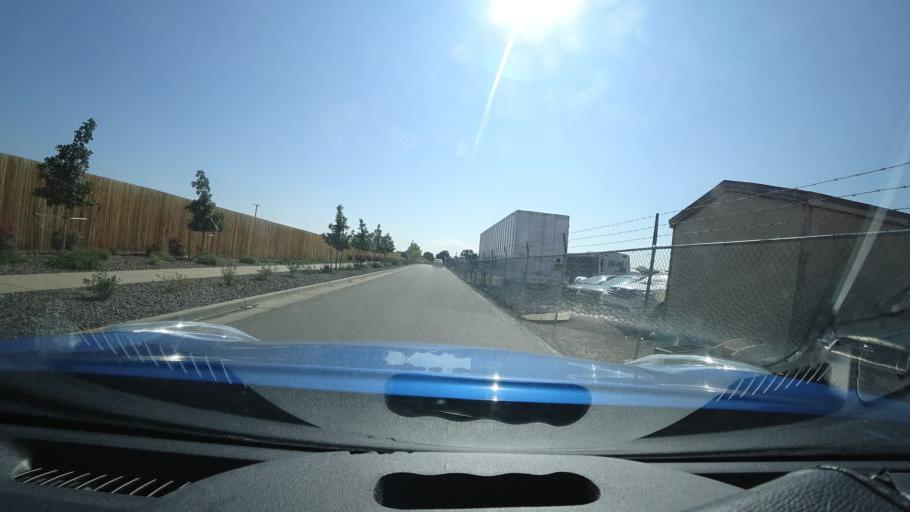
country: US
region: Colorado
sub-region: Adams County
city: Aurora
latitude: 39.7221
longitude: -104.7975
